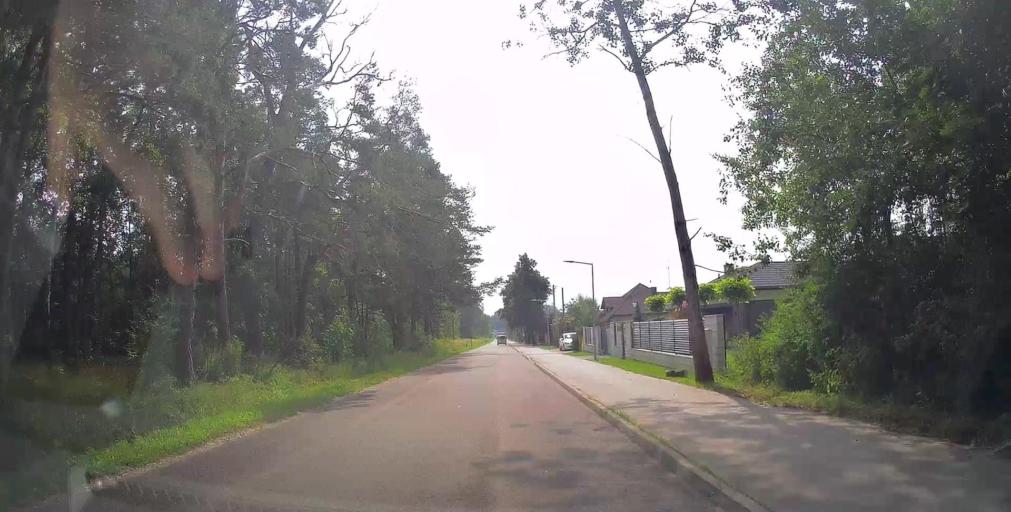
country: PL
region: Masovian Voivodeship
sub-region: Powiat bialobrzeski
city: Sucha
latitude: 51.6279
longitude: 20.9537
